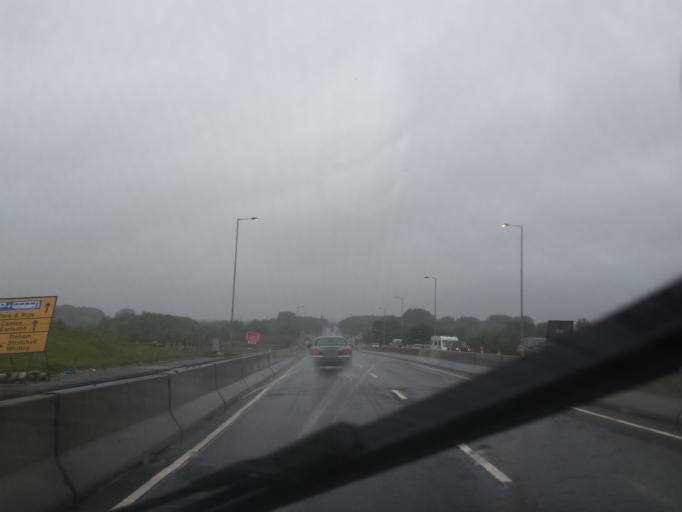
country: GB
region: England
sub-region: Coventry
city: Coventry
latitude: 52.3771
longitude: -1.4876
